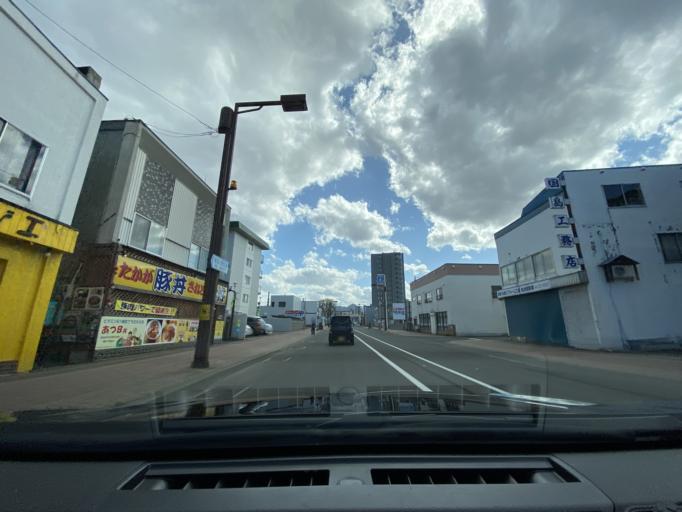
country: JP
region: Hokkaido
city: Sapporo
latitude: 43.0895
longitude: 141.3176
